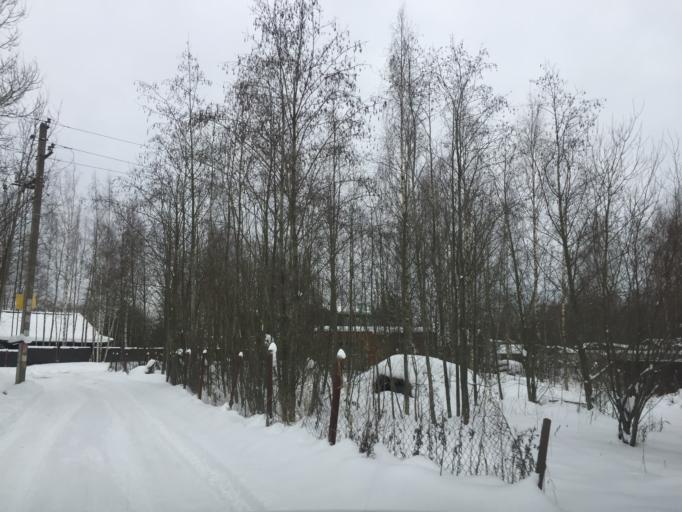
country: RU
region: Leningrad
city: Otradnoye
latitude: 59.7834
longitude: 30.7874
